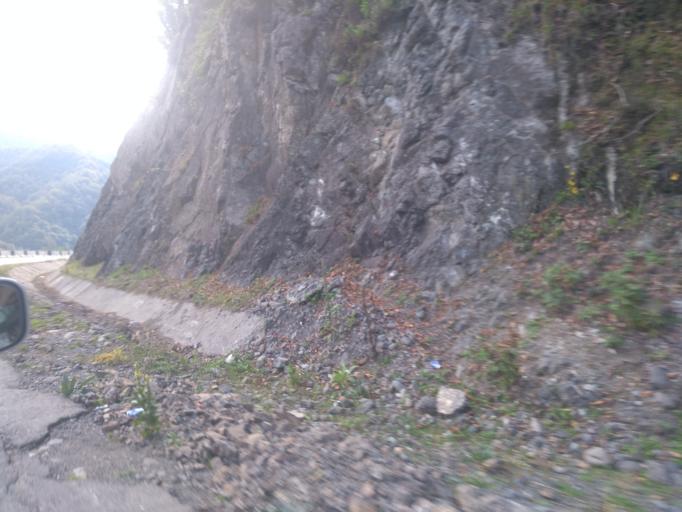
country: TR
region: Artvin
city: Muratli
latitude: 41.5536
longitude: 41.8029
